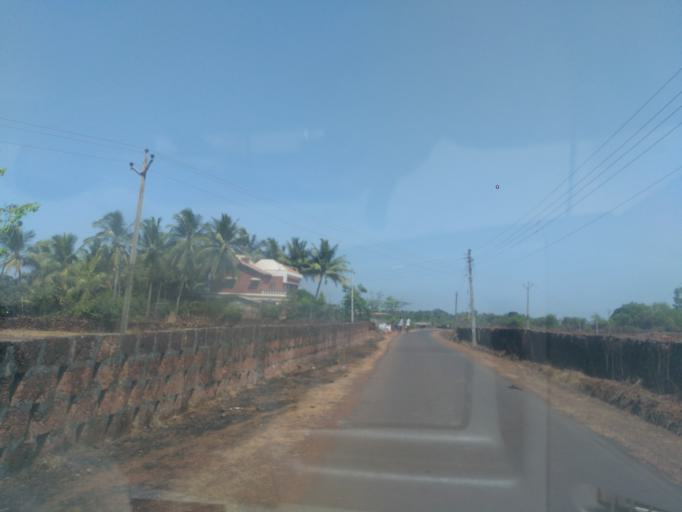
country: IN
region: Maharashtra
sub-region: Ratnagiri
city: Makhjan
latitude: 17.2408
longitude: 73.2696
